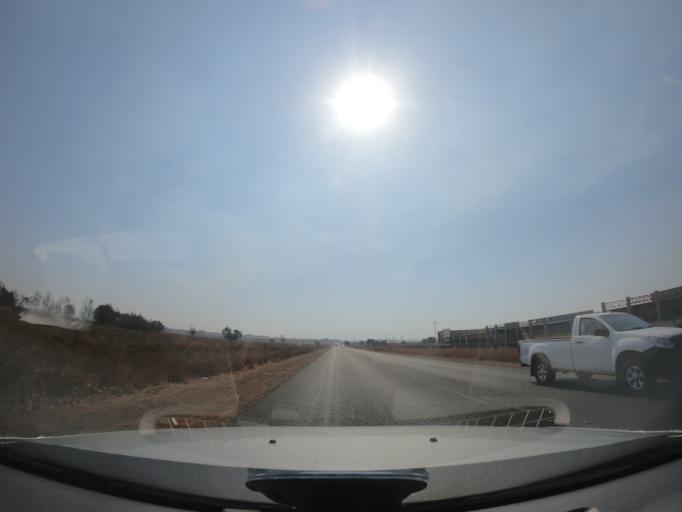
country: ZA
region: Mpumalanga
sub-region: Nkangala District Municipality
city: Middelburg
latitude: -25.8161
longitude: 29.4615
